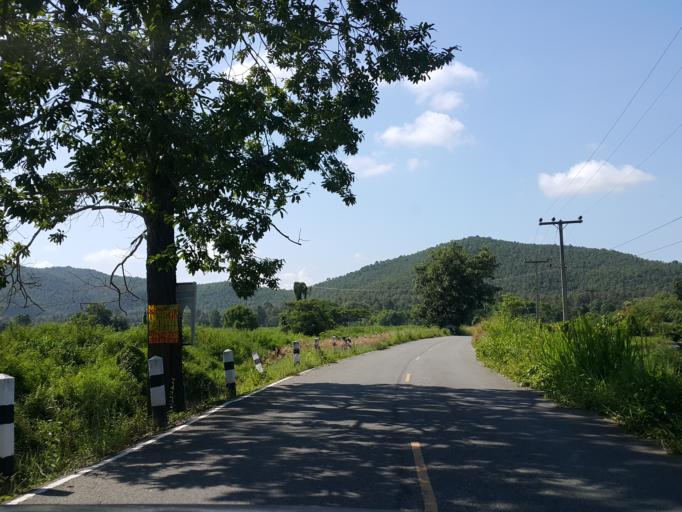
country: TH
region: Chiang Mai
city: Mae On
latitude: 18.7835
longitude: 99.1840
